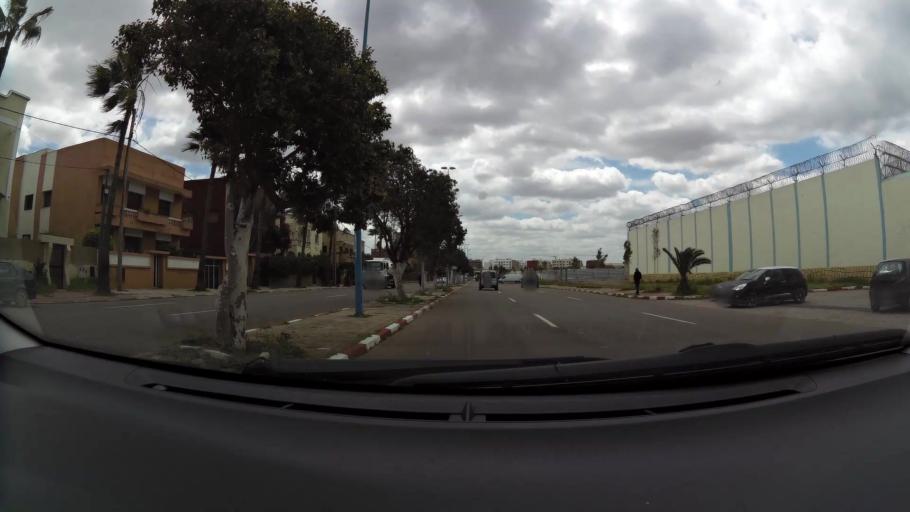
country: MA
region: Grand Casablanca
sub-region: Casablanca
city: Casablanca
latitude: 33.6107
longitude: -7.5495
